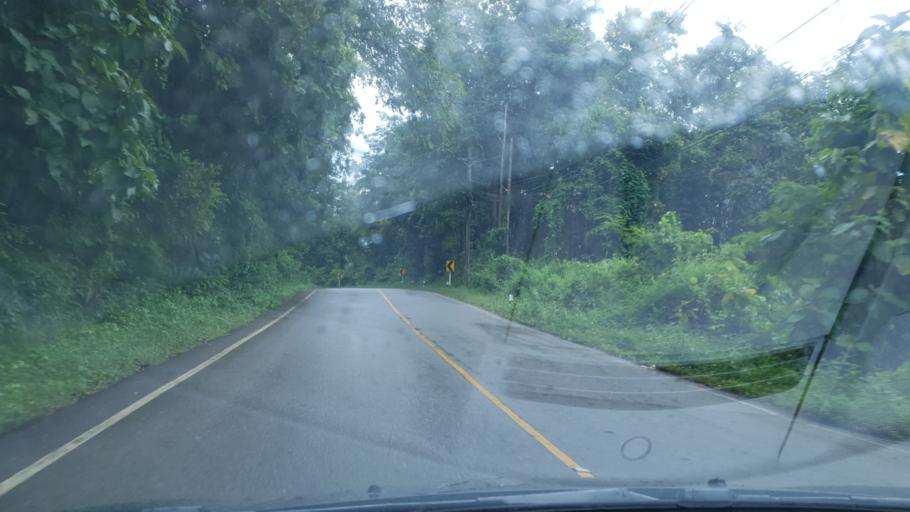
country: TH
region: Mae Hong Son
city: Pa Pae
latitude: 18.2796
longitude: 97.9386
